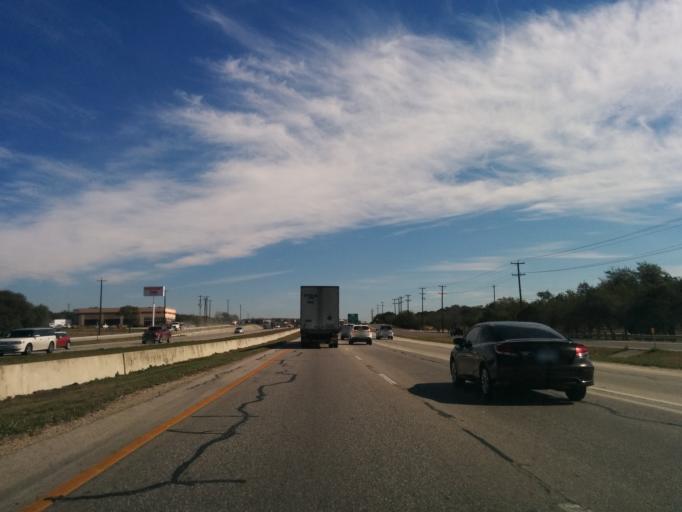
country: US
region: Texas
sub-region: Bexar County
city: Shavano Park
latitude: 29.5956
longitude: -98.5723
